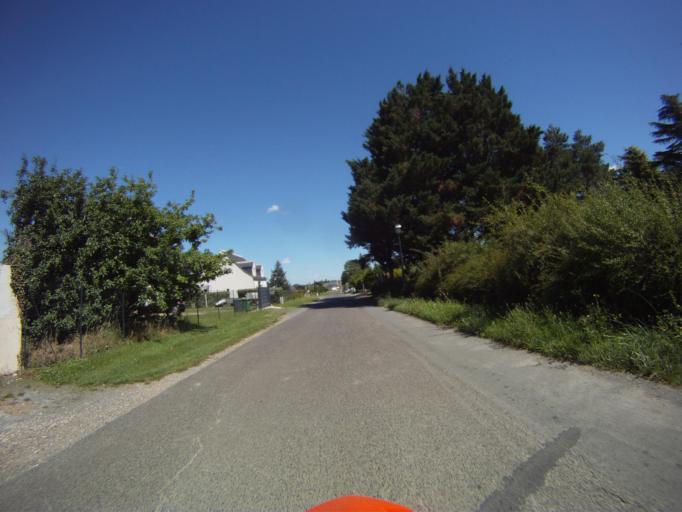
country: FR
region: Centre
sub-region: Departement d'Indre-et-Loire
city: Rochecorbon
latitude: 47.4224
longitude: 0.7738
